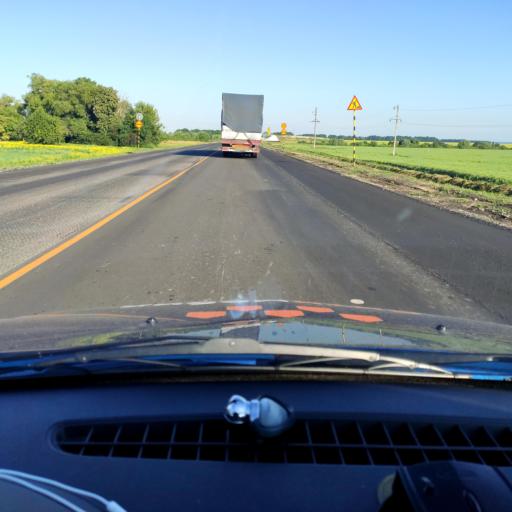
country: RU
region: Orjol
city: Zmiyevka
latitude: 52.6969
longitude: 36.3846
